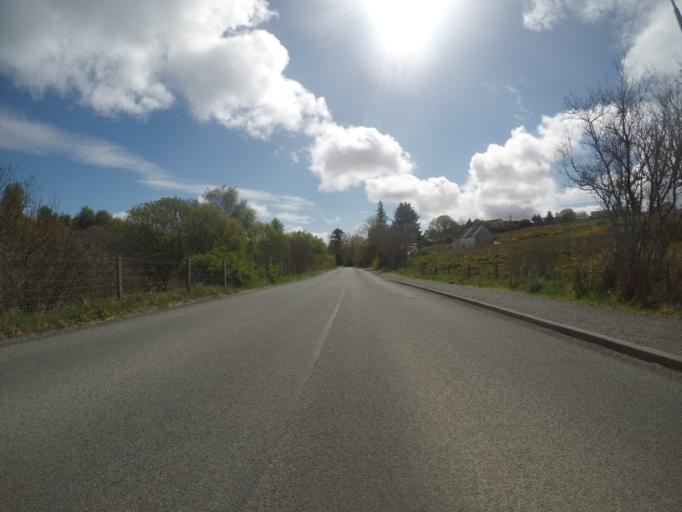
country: GB
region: Scotland
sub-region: Highland
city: Portree
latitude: 57.4191
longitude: -6.1927
